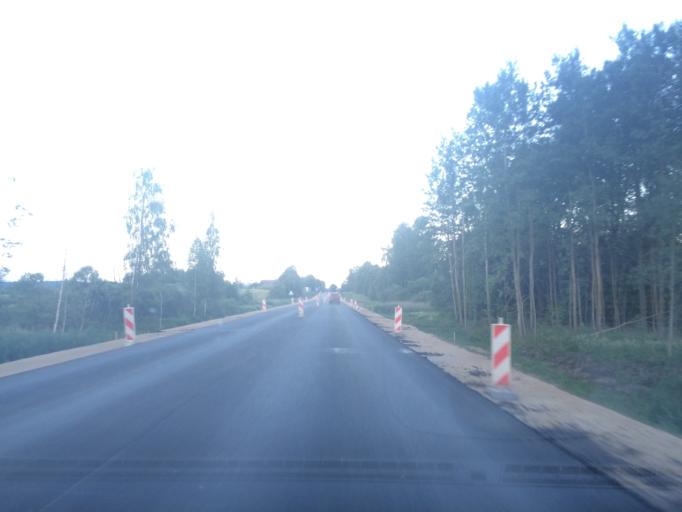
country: LT
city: Zarasai
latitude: 55.7496
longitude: 26.3172
